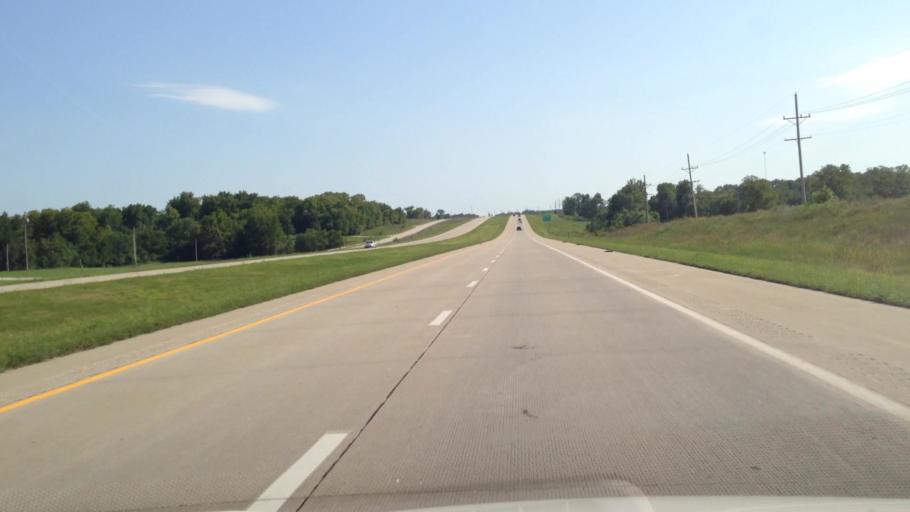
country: US
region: Kansas
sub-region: Linn County
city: Pleasanton
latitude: 38.2053
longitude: -94.7056
